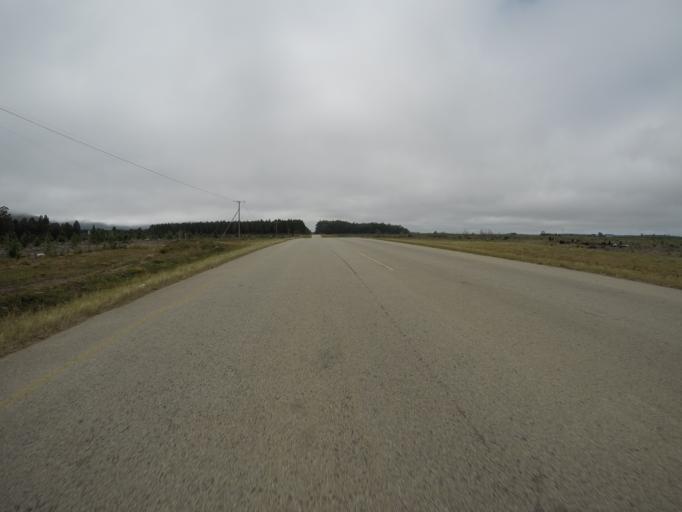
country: ZA
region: Eastern Cape
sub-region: Cacadu District Municipality
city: Kareedouw
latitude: -33.9939
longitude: 24.1008
